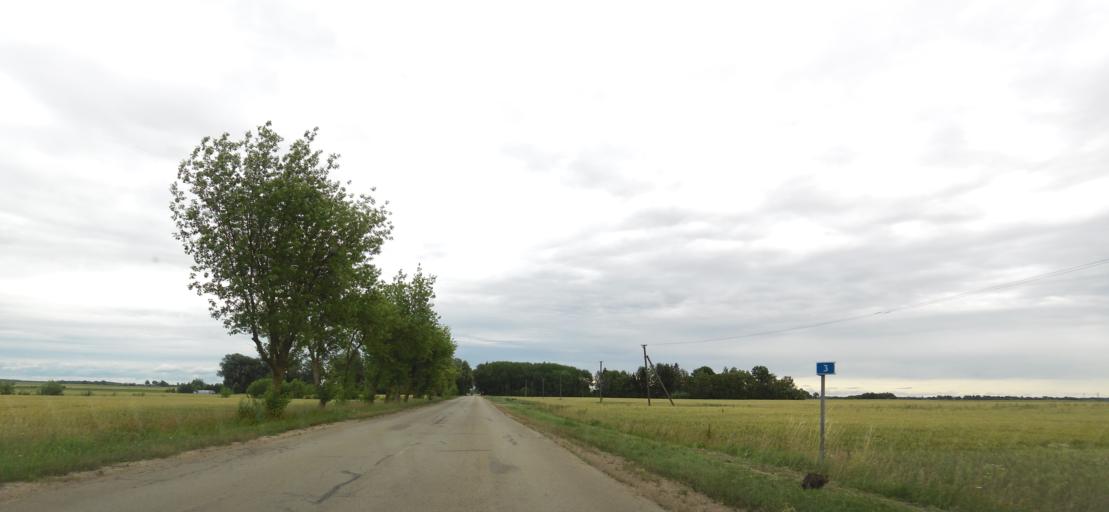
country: LT
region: Panevezys
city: Pasvalys
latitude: 56.0879
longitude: 24.4937
